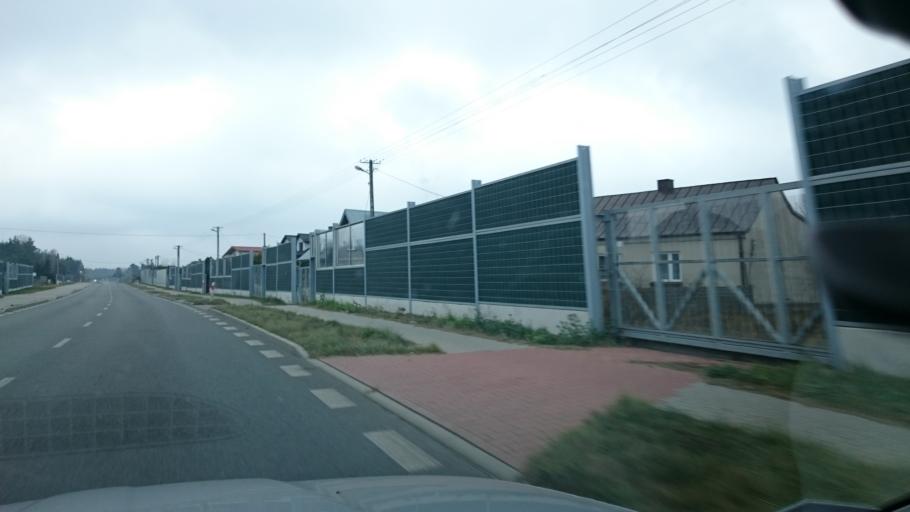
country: PL
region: Swietokrzyskie
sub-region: Powiat konecki
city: Konskie
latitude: 51.1596
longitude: 20.3683
